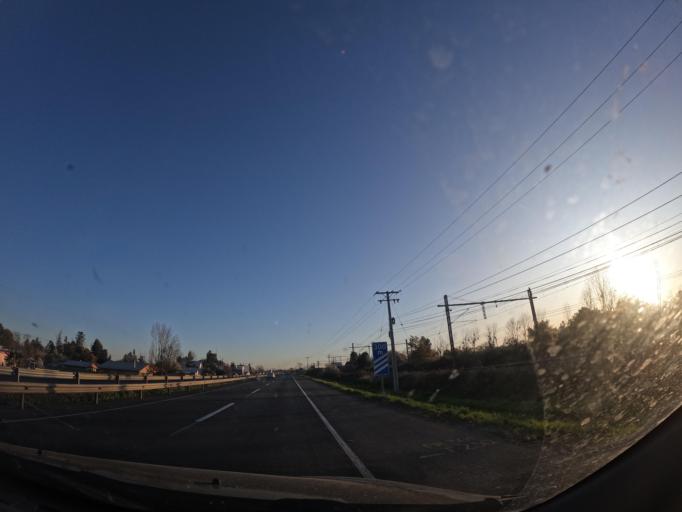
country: CL
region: Biobio
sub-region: Provincia de Nuble
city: San Carlos
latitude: -36.4771
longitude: -72.0130
